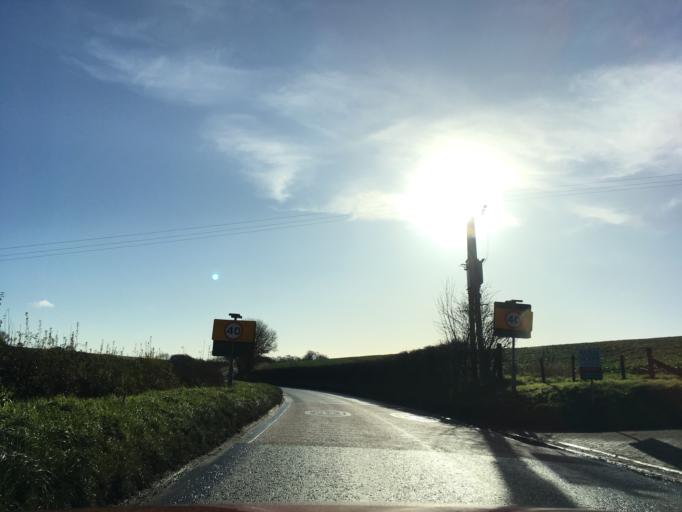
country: GB
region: England
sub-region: Wiltshire
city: Collingbourne Kingston
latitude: 51.2960
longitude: -1.6574
